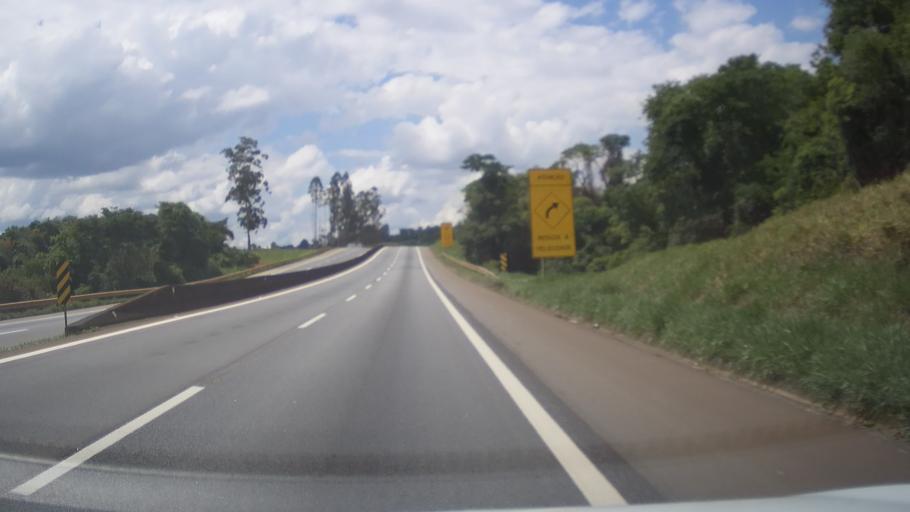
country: BR
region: Minas Gerais
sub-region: Nepomuceno
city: Nepomuceno
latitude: -21.2928
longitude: -45.1485
